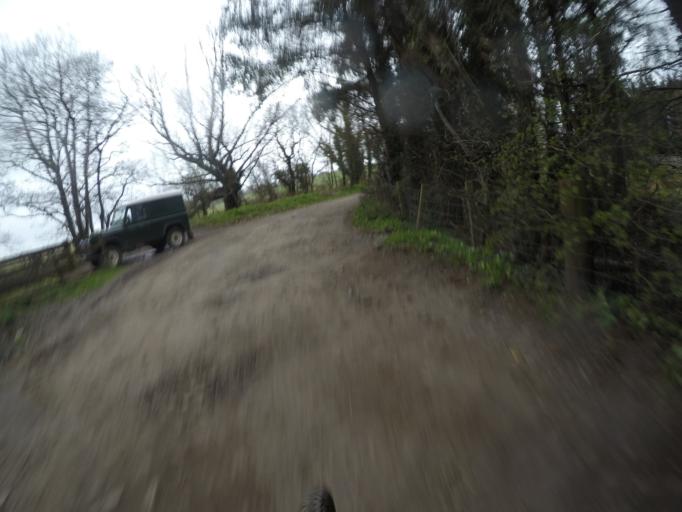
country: GB
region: Scotland
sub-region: East Ayrshire
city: Galston
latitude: 55.6067
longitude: -4.4090
